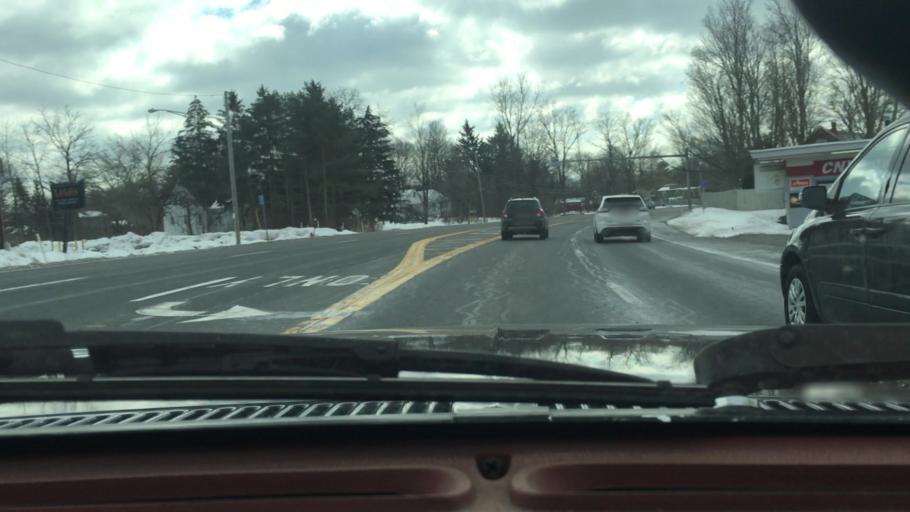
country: US
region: New York
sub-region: Onondaga County
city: Liverpool
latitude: 43.1583
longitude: -76.2286
